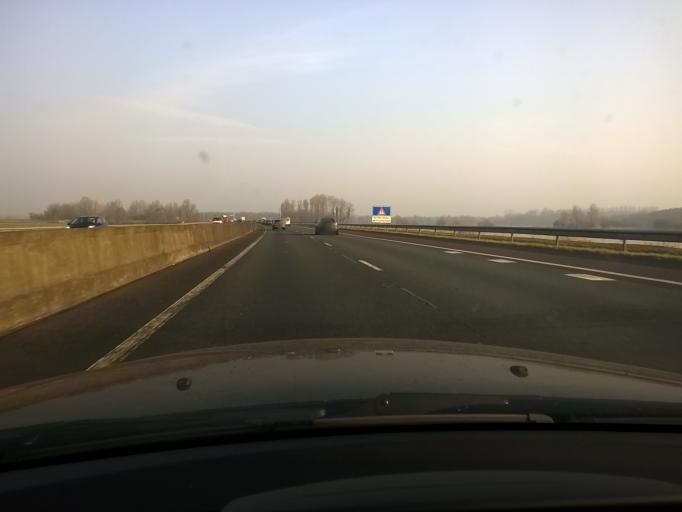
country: NL
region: Groningen
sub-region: Gemeente Haren
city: Haren
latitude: 53.1433
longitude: 6.6076
